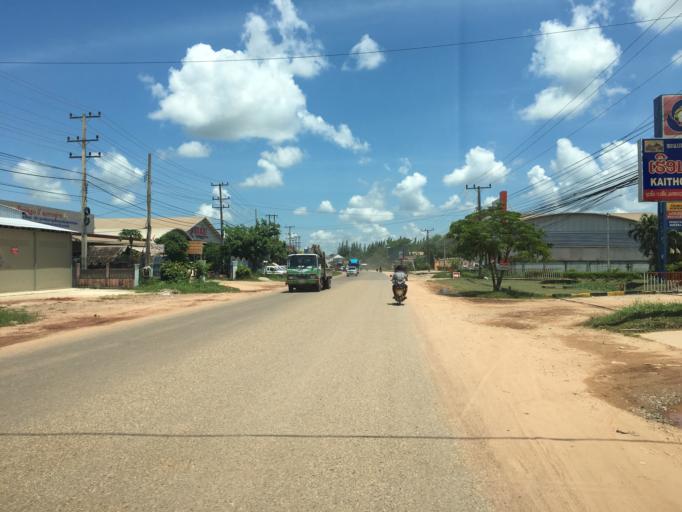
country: LA
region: Vientiane
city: Vientiane
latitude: 18.0310
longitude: 102.5479
